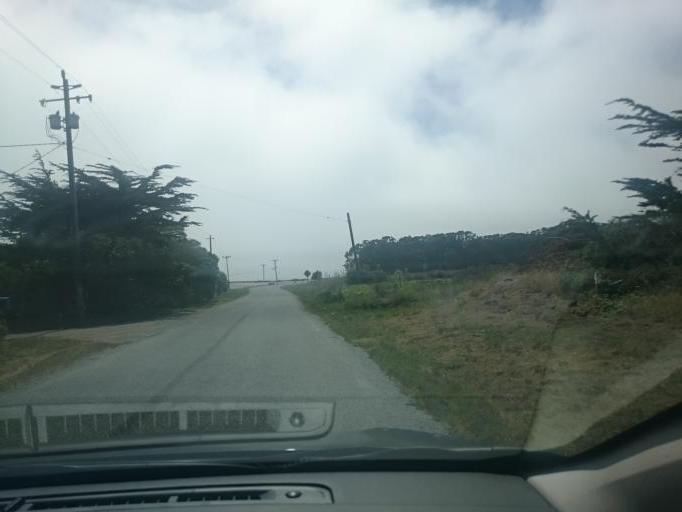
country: US
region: California
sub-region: San Mateo County
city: Portola Valley
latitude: 37.1854
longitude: -122.3878
